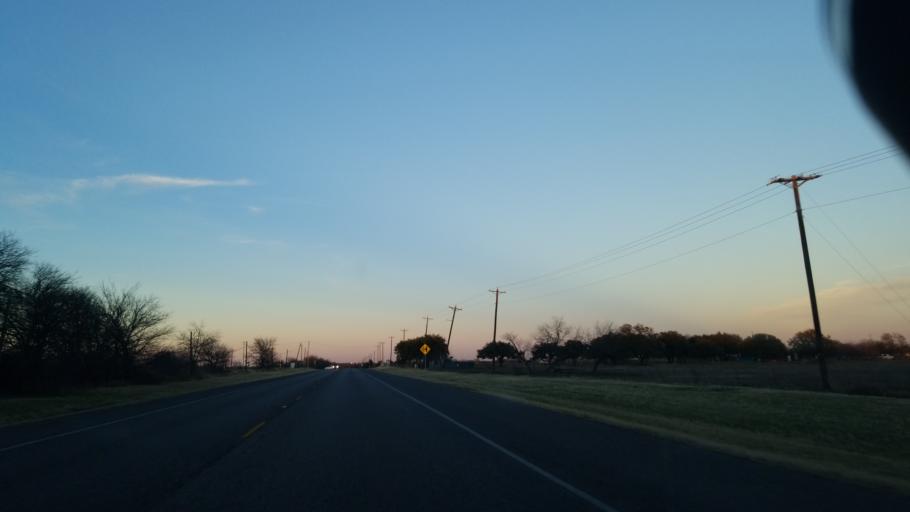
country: US
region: Texas
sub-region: Denton County
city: Argyle
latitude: 33.1479
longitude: -97.1691
